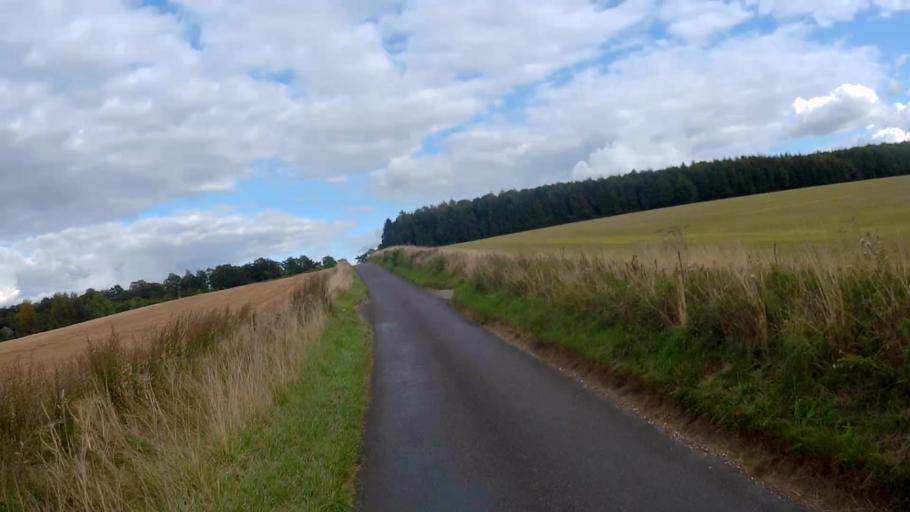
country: GB
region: England
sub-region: Hampshire
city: Kings Worthy
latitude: 51.1471
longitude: -1.2880
